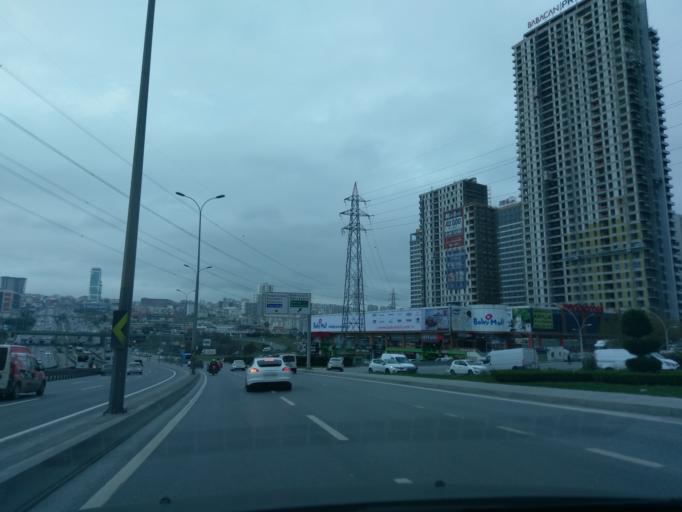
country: TR
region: Istanbul
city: Yakuplu
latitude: 41.0058
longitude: 28.6830
